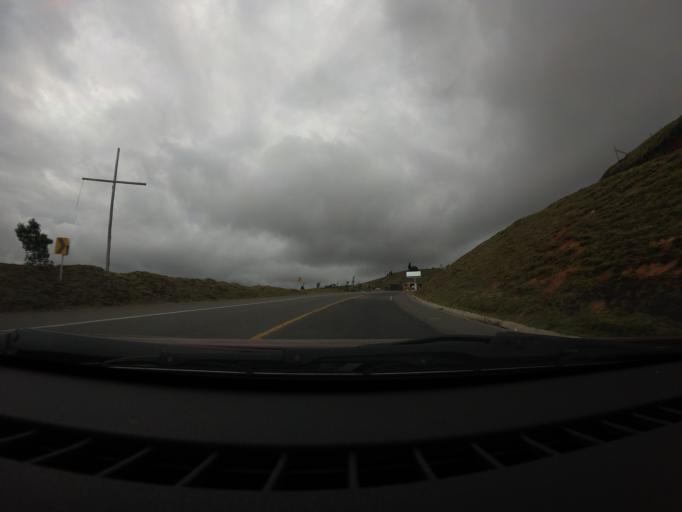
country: CO
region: Boyaca
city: Tunja
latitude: 5.4945
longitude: -73.3831
